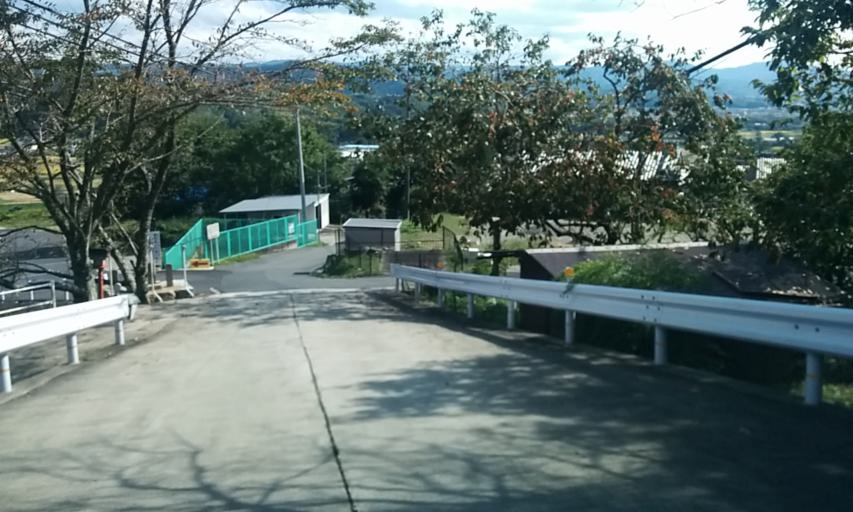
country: JP
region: Nara
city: Nara-shi
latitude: 34.7733
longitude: 135.8647
